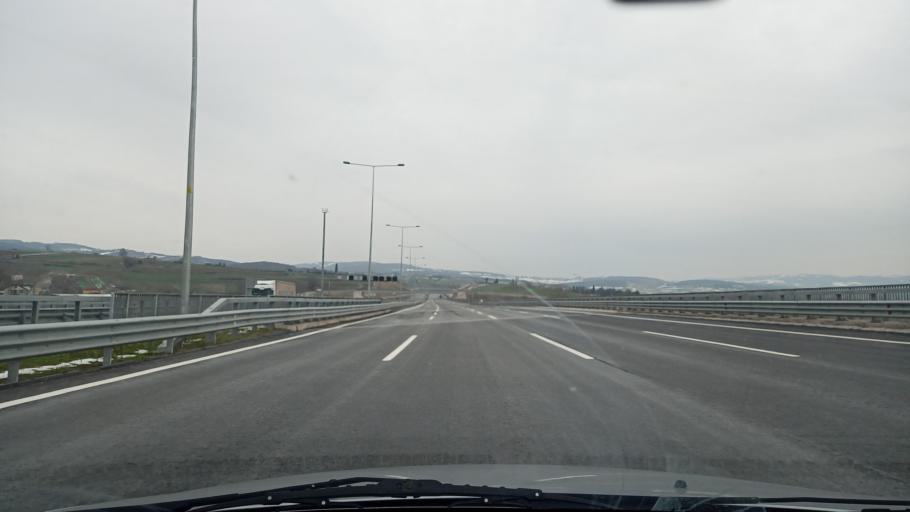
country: TR
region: Kocaeli
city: Kosekoy
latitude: 40.7919
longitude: 30.0411
